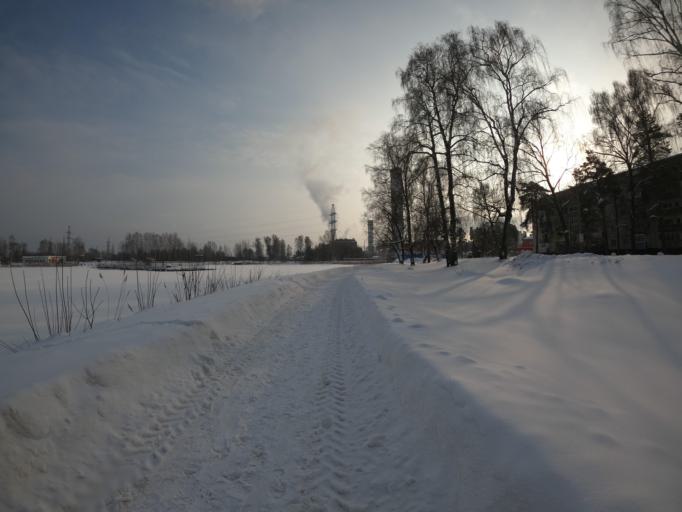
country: RU
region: Moskovskaya
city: Elektrogorsk
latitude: 55.8918
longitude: 38.7790
